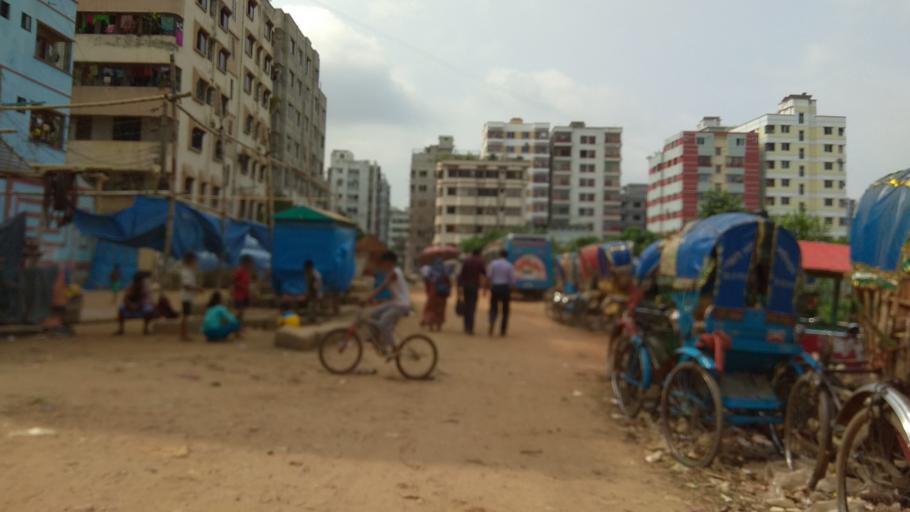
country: BD
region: Dhaka
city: Azimpur
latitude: 23.8122
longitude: 90.3550
